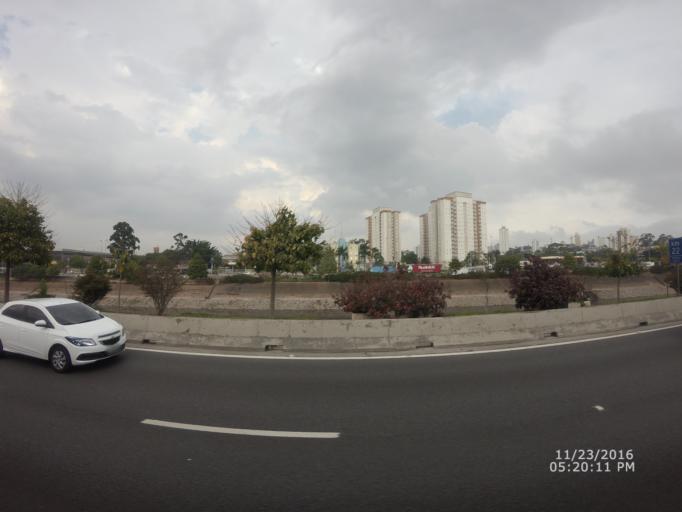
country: BR
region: Sao Paulo
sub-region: Guarulhos
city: Guarulhos
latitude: -23.5196
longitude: -46.5564
